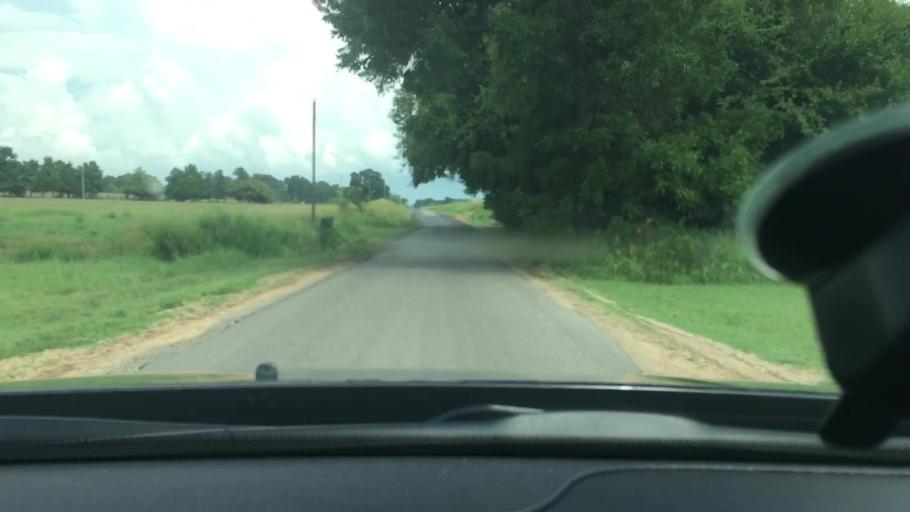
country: US
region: Oklahoma
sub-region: Carter County
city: Dickson
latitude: 34.2030
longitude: -96.8983
